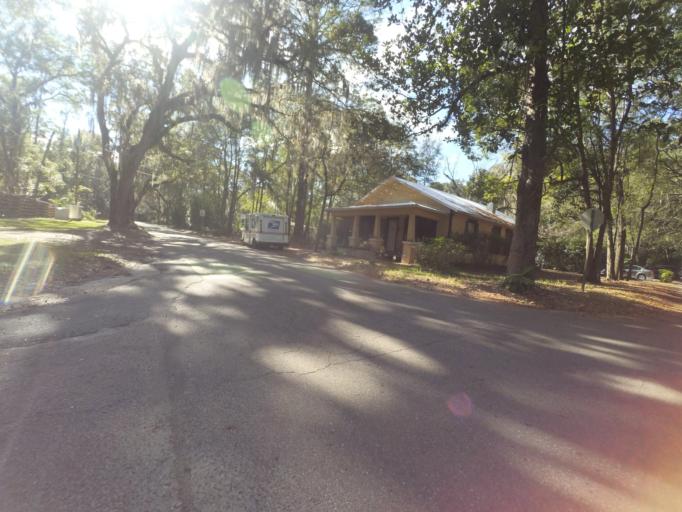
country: US
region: Florida
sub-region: Alachua County
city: Gainesville
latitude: 29.6649
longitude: -82.3370
